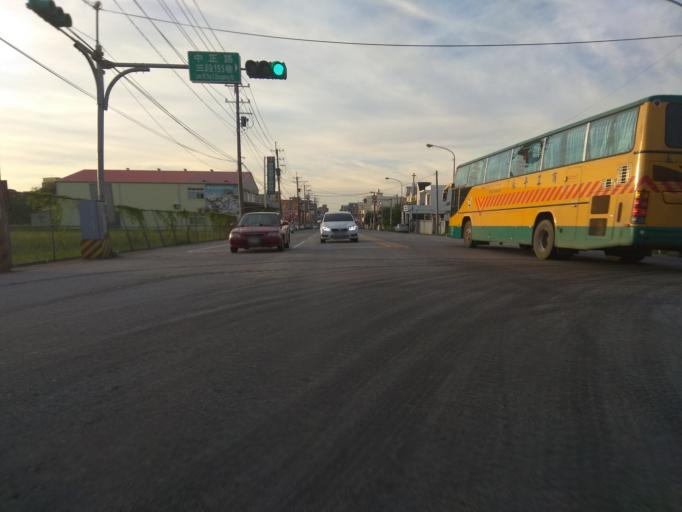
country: TW
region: Taiwan
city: Taoyuan City
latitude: 24.9863
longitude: 121.1845
